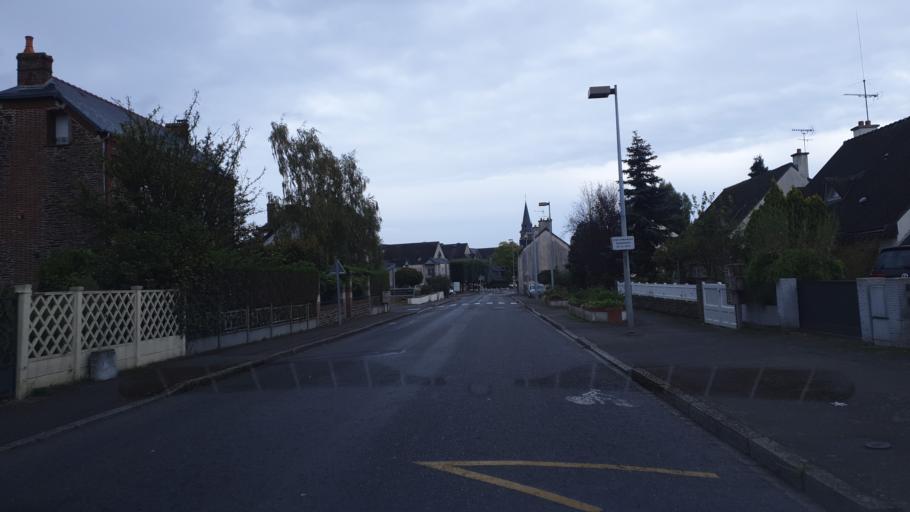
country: FR
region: Brittany
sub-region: Departement d'Ille-et-Vilaine
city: Chartres-de-Bretagne
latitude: 48.0420
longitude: -1.7110
